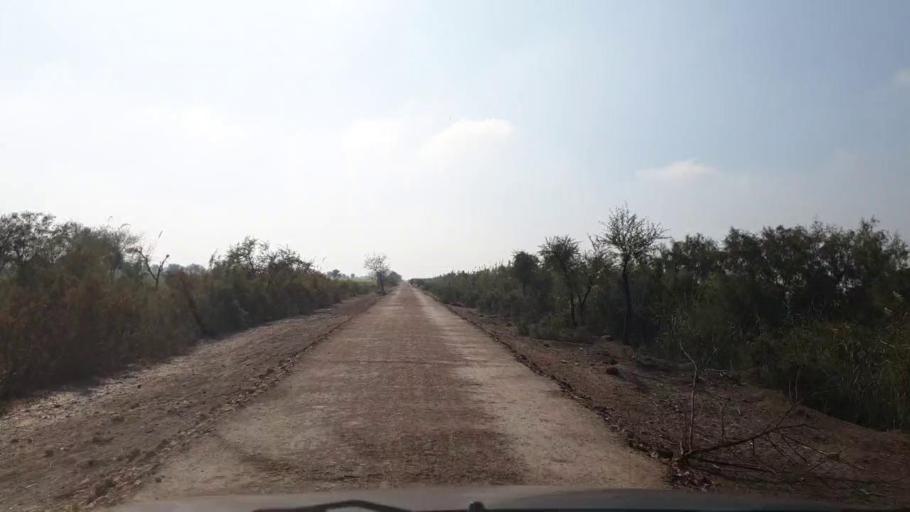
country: PK
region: Sindh
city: Sinjhoro
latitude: 26.0526
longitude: 68.7780
